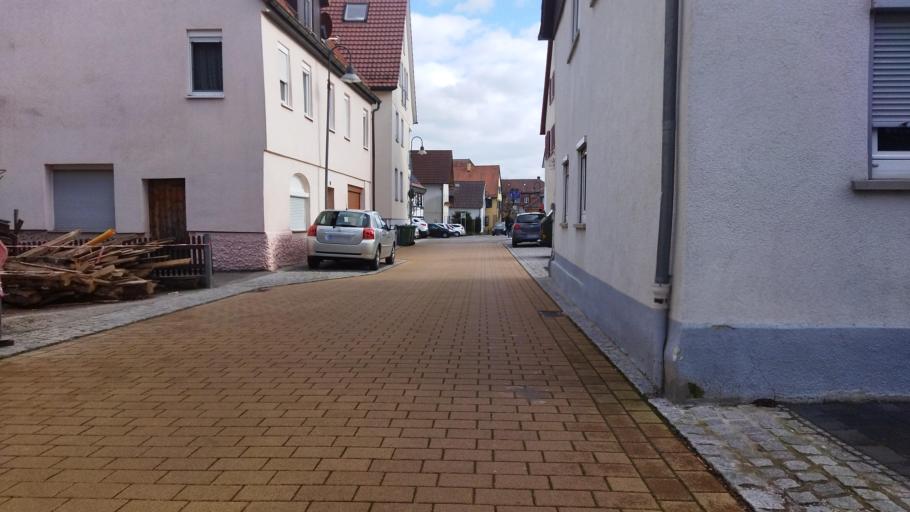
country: DE
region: Baden-Wuerttemberg
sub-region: Regierungsbezirk Stuttgart
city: Freudental
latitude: 49.0100
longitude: 9.0594
